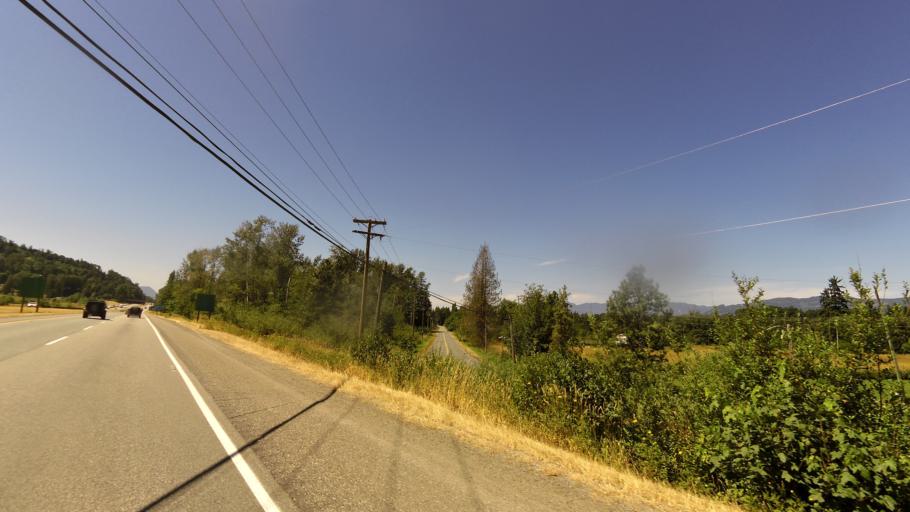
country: CA
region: British Columbia
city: Agassiz
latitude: 49.1860
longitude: -121.7499
